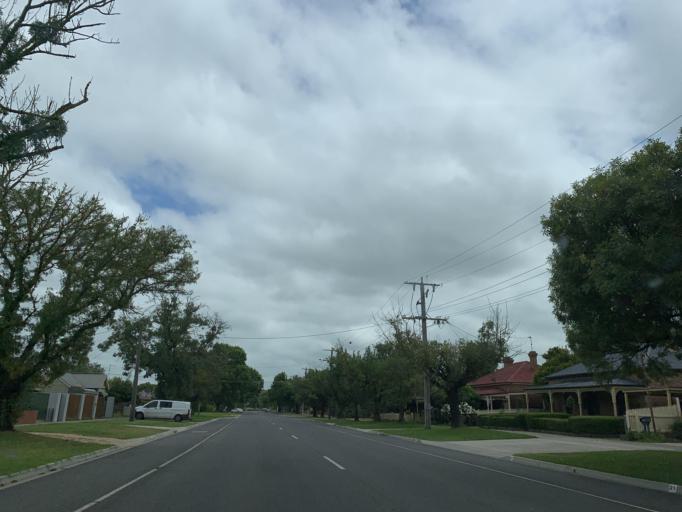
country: AU
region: Victoria
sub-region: Wellington
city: Sale
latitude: -37.9639
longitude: 146.9790
